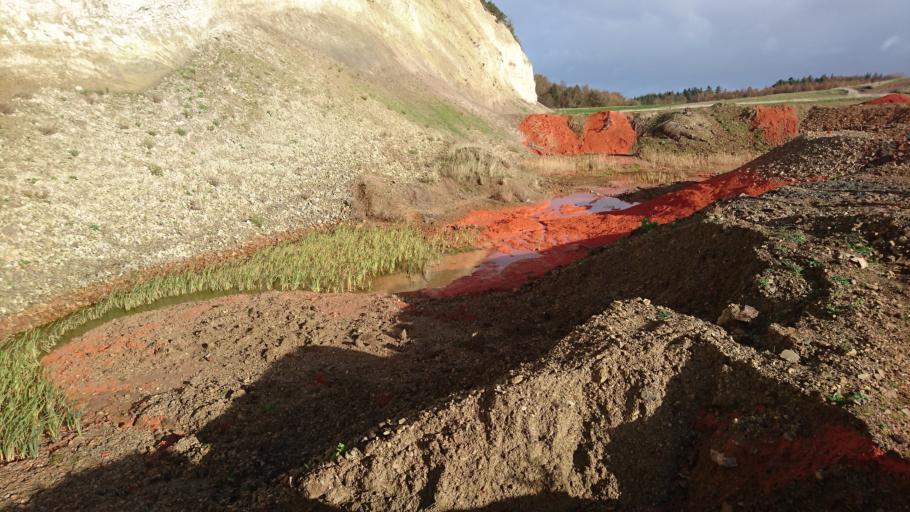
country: DK
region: North Denmark
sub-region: Morso Kommune
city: Nykobing Mors
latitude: 56.8351
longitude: 9.0023
